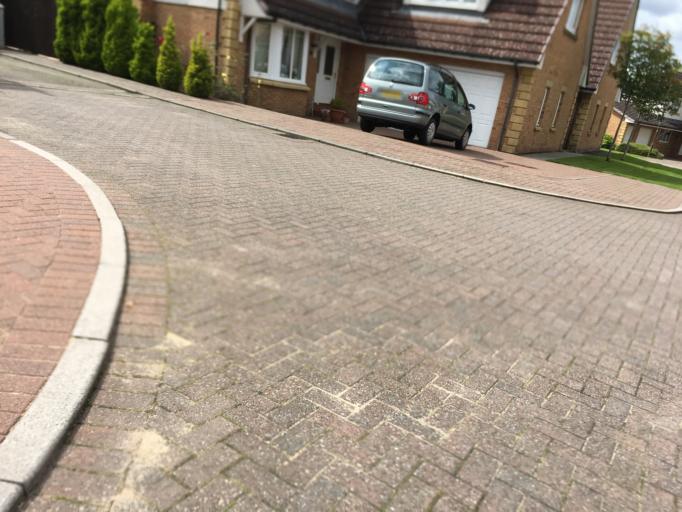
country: GB
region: Scotland
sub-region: West Lothian
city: Livingston
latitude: 55.8714
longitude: -3.5121
